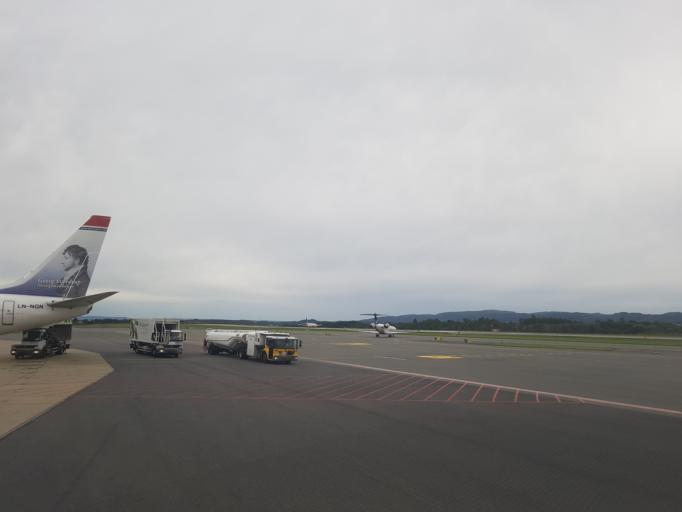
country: NO
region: Hordaland
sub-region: Bergen
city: Ytrebygda
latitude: 60.2893
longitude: 5.2249
